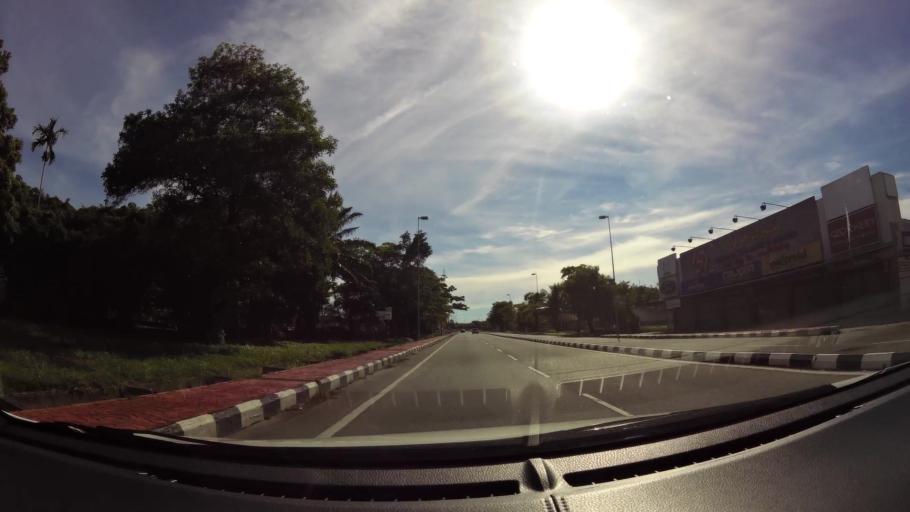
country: BN
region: Belait
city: Kuala Belait
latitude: 4.5775
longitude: 114.2037
